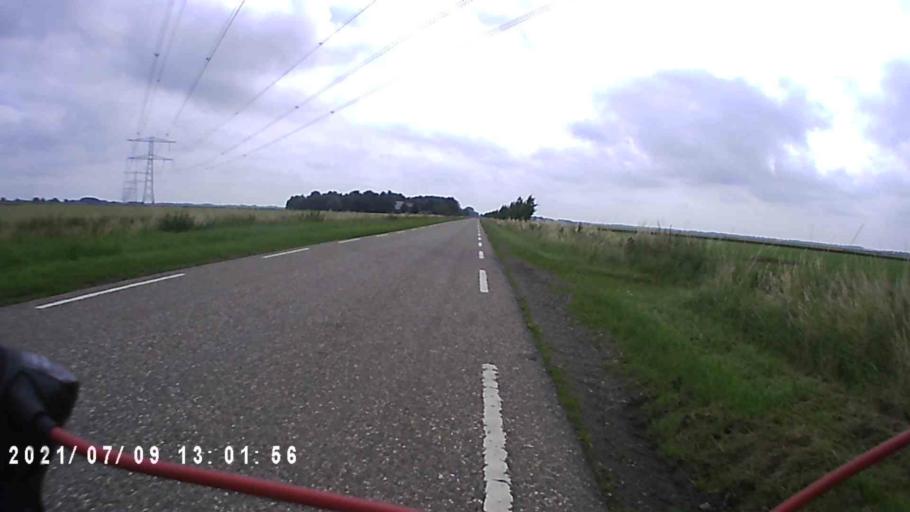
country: NL
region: Groningen
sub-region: Gemeente  Oldambt
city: Winschoten
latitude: 53.1349
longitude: 7.0810
